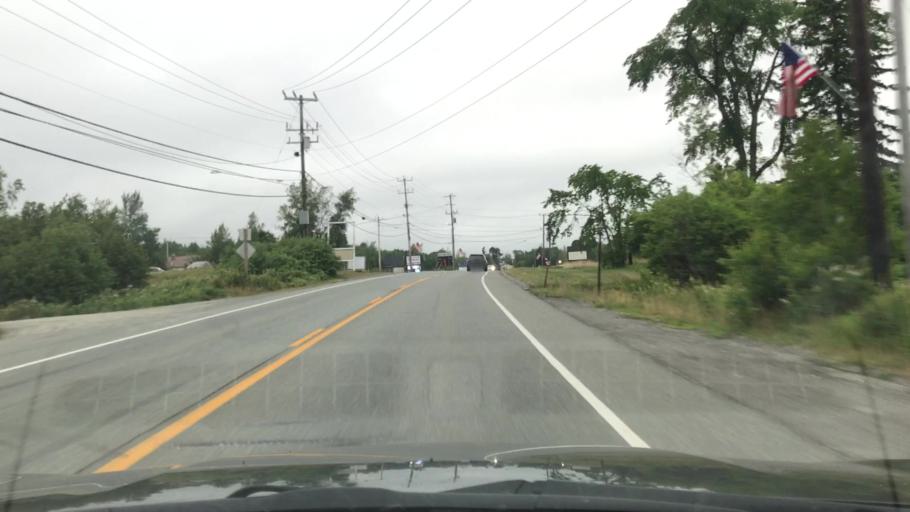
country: US
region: Maine
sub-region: Hancock County
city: Trenton
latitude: 44.4329
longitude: -68.3686
